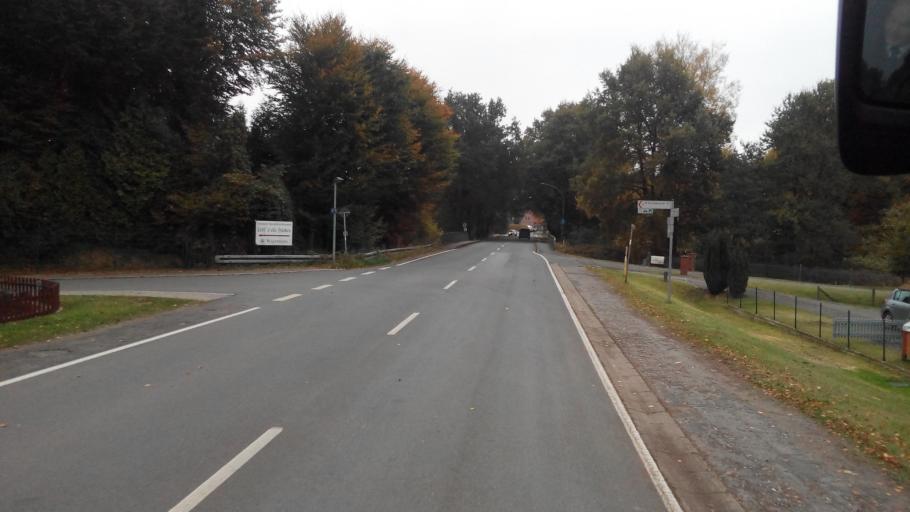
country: DE
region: North Rhine-Westphalia
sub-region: Regierungsbezirk Munster
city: Haltern
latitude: 51.7669
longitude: 7.2284
